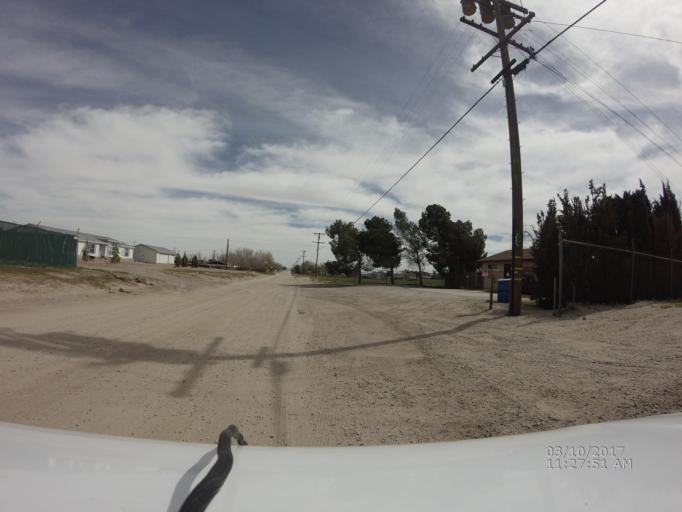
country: US
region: California
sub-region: Los Angeles County
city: Quartz Hill
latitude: 34.7546
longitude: -118.2881
